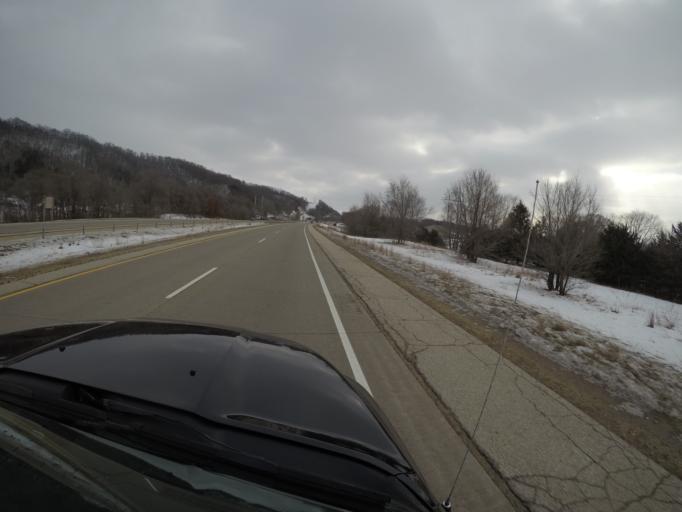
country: US
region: Wisconsin
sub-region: La Crosse County
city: Onalaska
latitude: 43.8970
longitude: -91.2194
